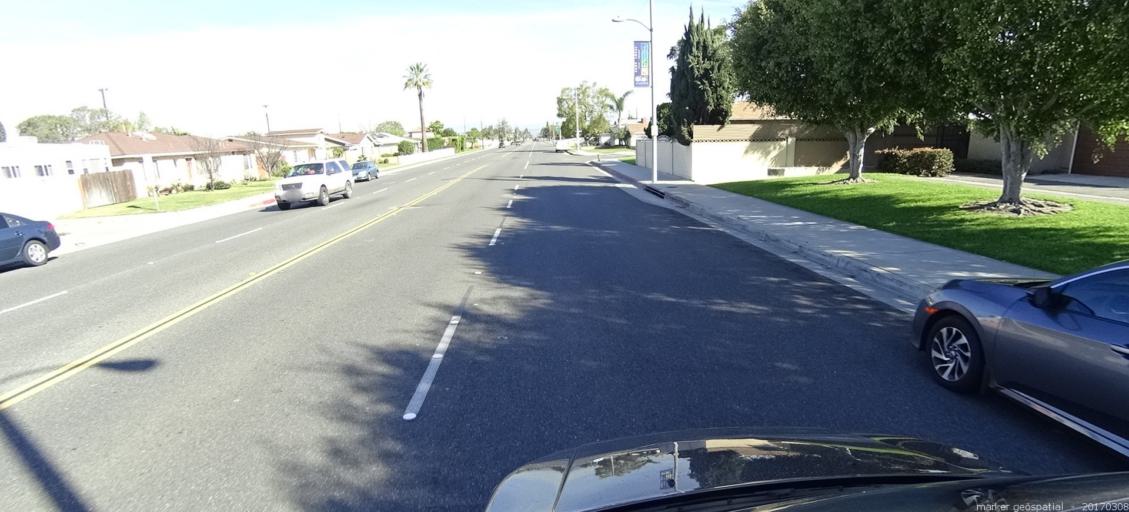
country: US
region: California
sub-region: Orange County
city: Stanton
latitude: 33.8116
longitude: -118.0020
